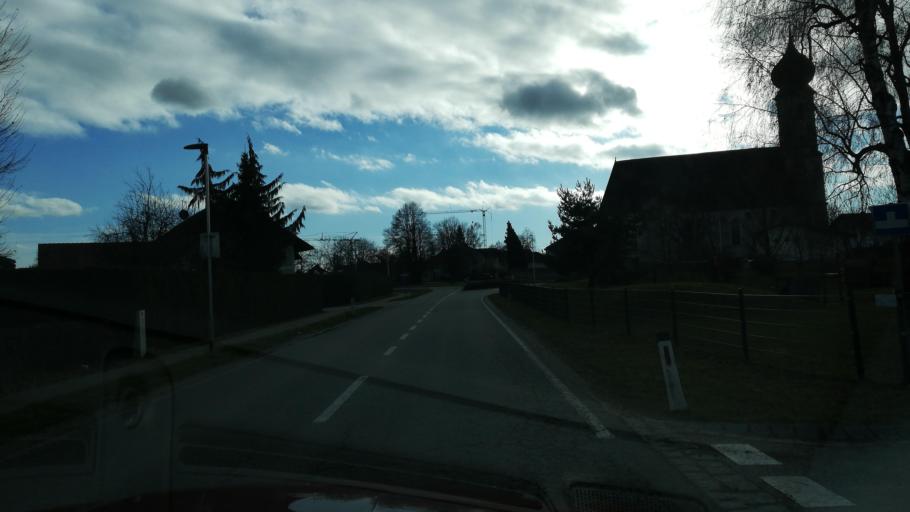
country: AT
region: Upper Austria
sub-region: Politischer Bezirk Braunau am Inn
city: Braunau am Inn
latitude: 48.2050
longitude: 13.1011
